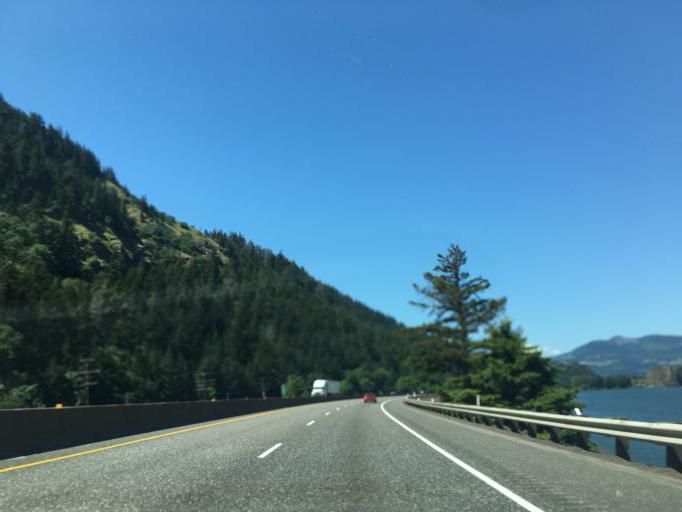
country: US
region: Washington
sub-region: Klickitat County
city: White Salmon
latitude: 45.6961
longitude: -121.4566
